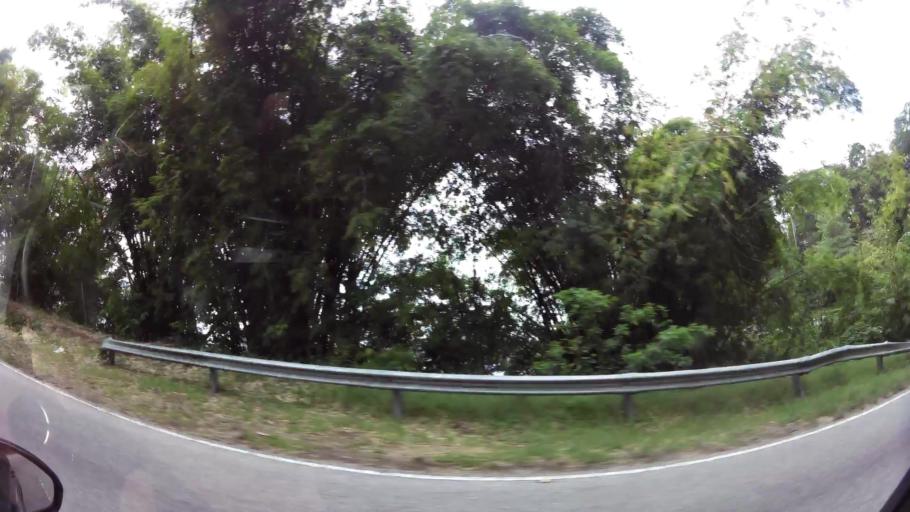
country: TT
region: City of Port of Spain
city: Port-of-Spain
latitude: 10.6718
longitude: -61.5076
